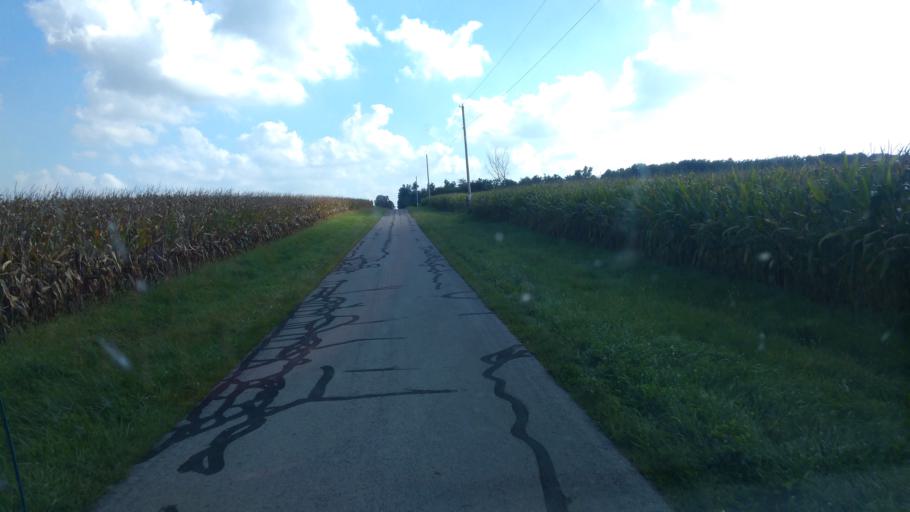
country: US
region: Ohio
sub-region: Hancock County
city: Arlington
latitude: 40.8465
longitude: -83.7085
